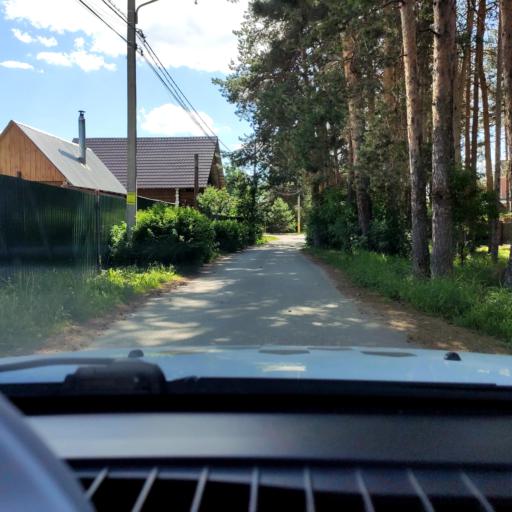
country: RU
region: Perm
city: Perm
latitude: 58.0577
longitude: 56.3061
